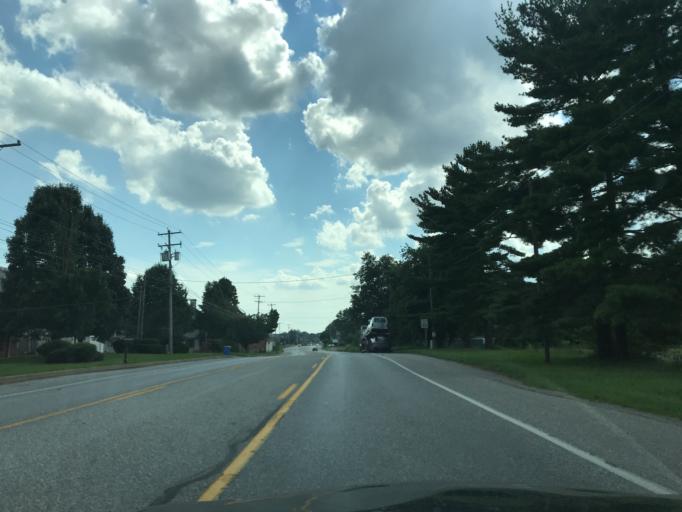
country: US
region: Pennsylvania
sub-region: York County
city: Stonybrook
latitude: 39.9884
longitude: -76.6423
